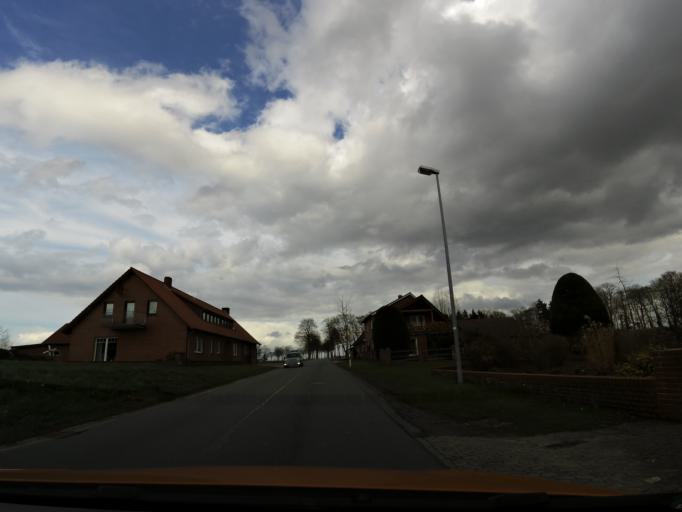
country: DE
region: Lower Saxony
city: Bassum
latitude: 52.8933
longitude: 8.7181
